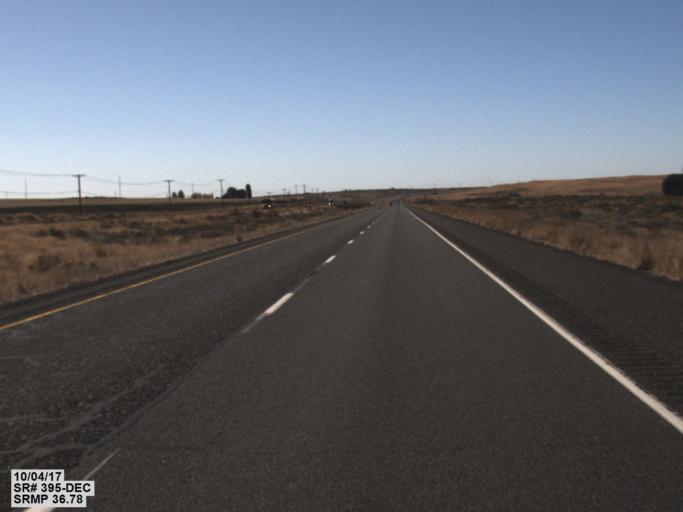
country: US
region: Washington
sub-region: Franklin County
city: Basin City
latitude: 46.4401
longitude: -119.0214
